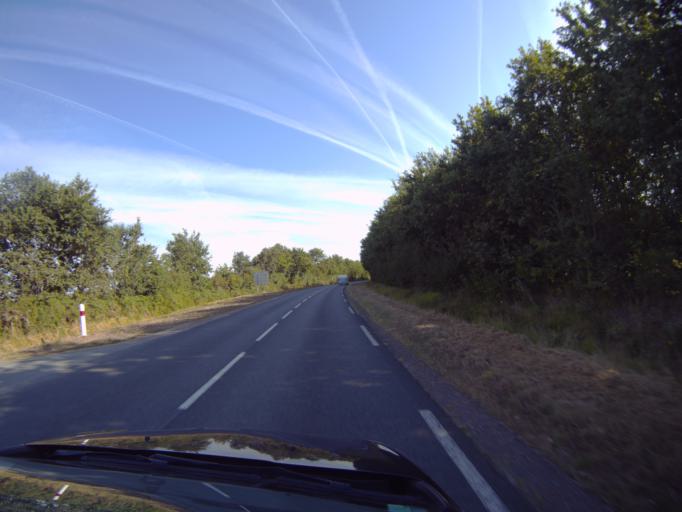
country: FR
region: Pays de la Loire
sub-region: Departement de la Vendee
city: Saint-Hilaire-de-Talmont
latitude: 46.4930
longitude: -1.5843
